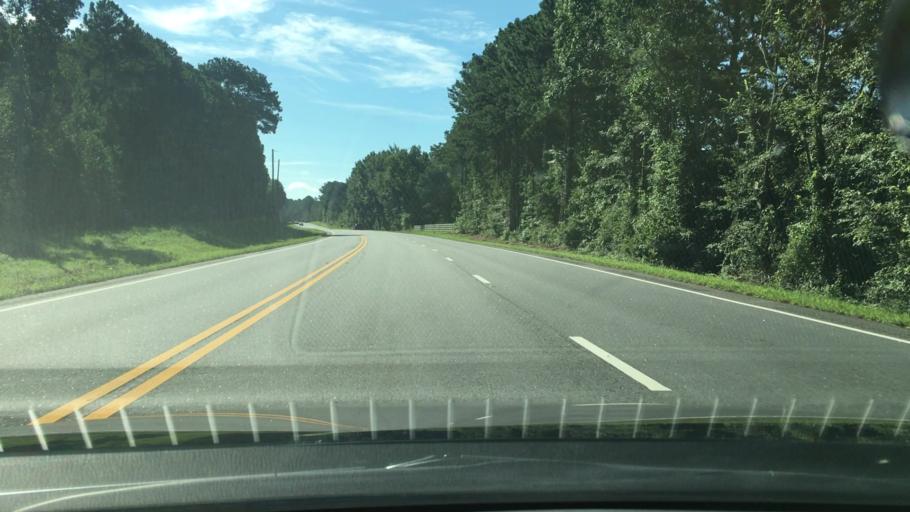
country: US
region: Georgia
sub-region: Putnam County
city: Jefferson
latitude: 33.4431
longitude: -83.4007
